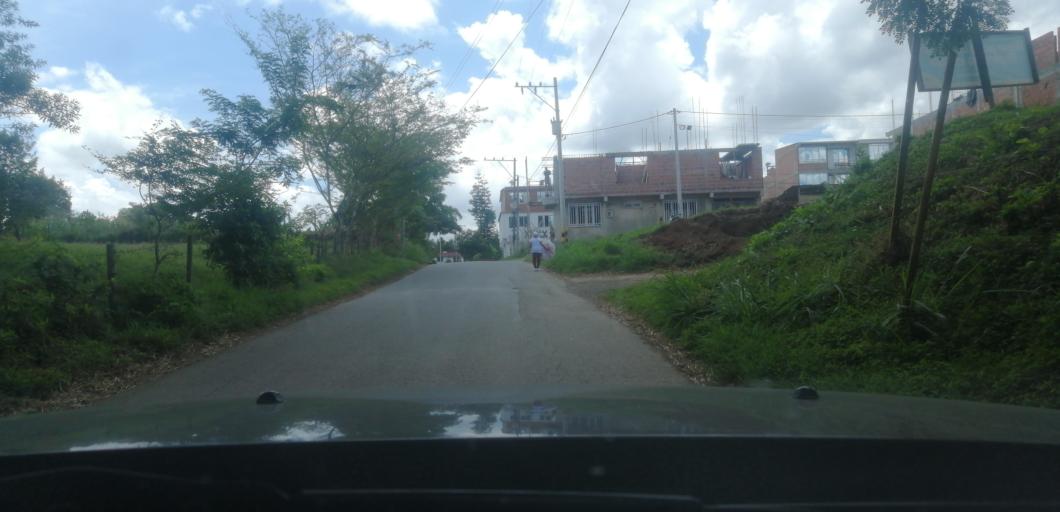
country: CO
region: Valle del Cauca
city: Restrepo
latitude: 3.8202
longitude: -76.5280
